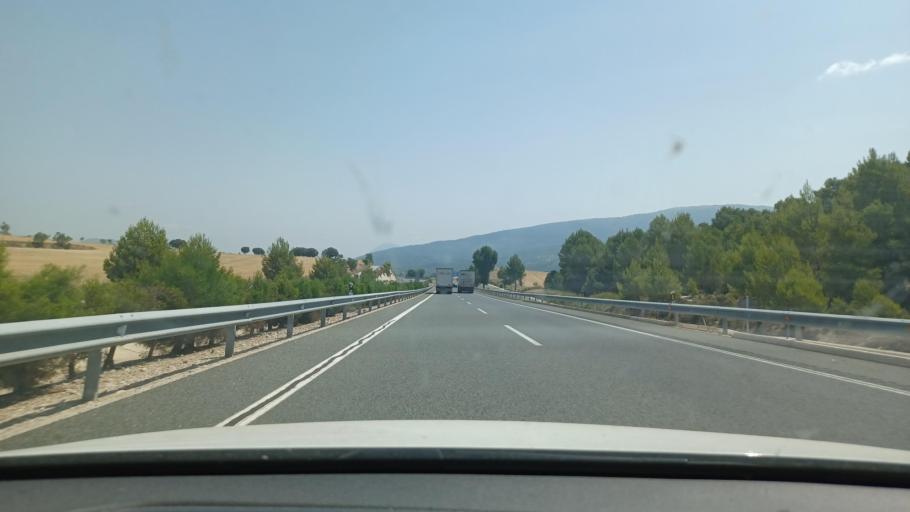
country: ES
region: Valencia
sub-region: Provincia de Alicante
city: Alcoy
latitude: 38.6399
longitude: -0.4975
